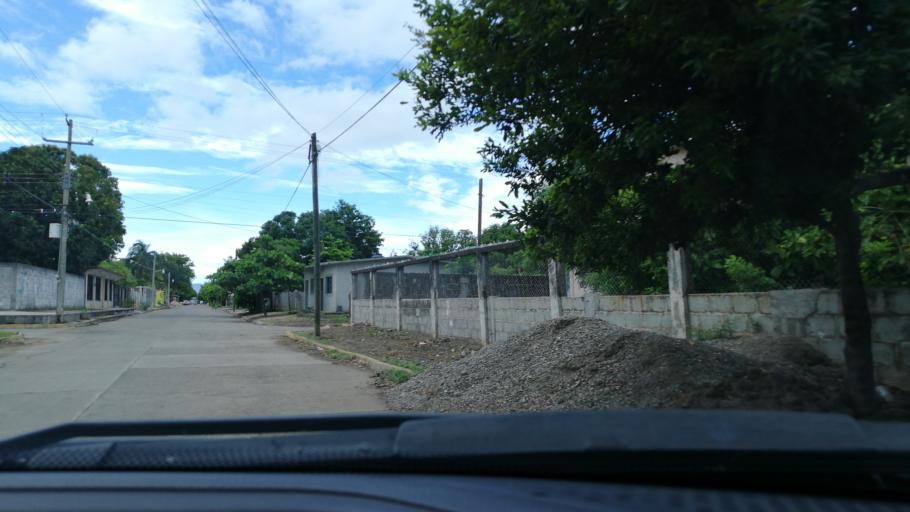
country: MX
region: Oaxaca
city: Asuncion Ixtaltepec
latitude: 16.5084
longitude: -95.0489
